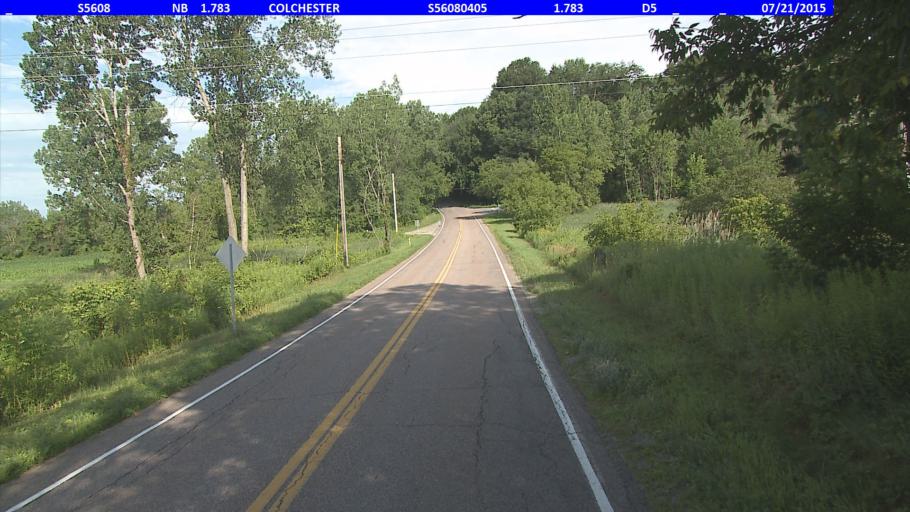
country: US
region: Vermont
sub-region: Chittenden County
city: Winooski
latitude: 44.5236
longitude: -73.2032
